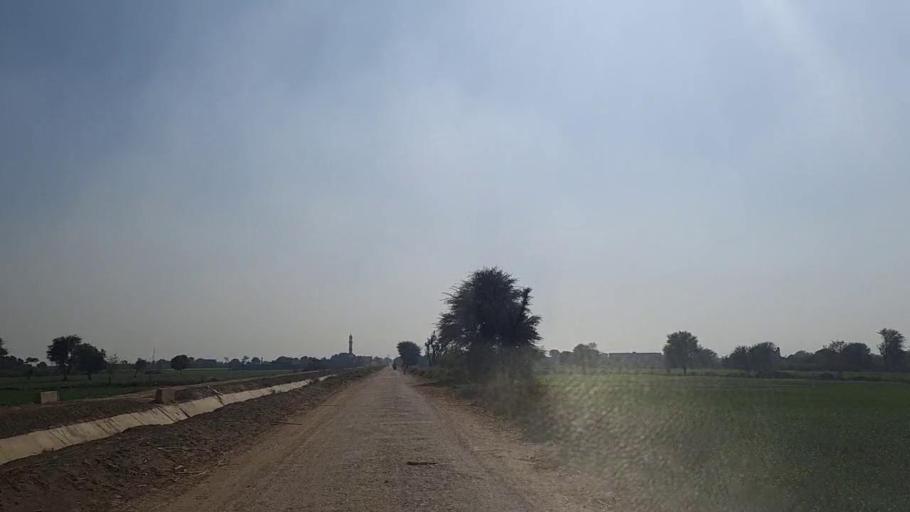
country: PK
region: Sindh
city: Shahpur Chakar
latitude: 26.1937
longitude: 68.5836
